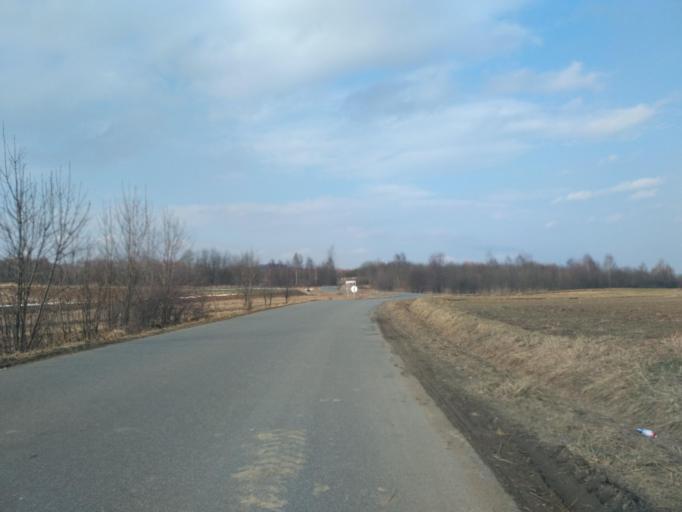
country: PL
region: Subcarpathian Voivodeship
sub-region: Powiat brzozowski
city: Gorki
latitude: 49.6558
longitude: 22.0315
